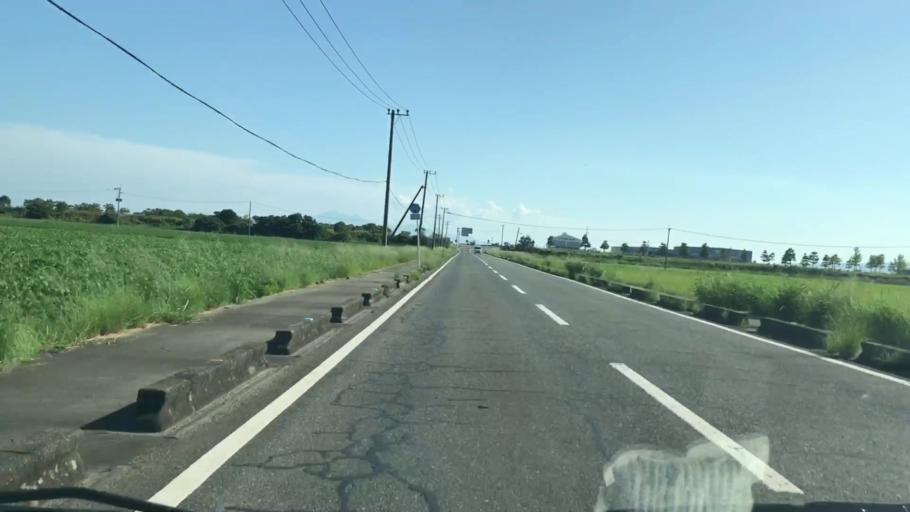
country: JP
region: Saga Prefecture
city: Okawa
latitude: 33.1562
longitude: 130.3081
